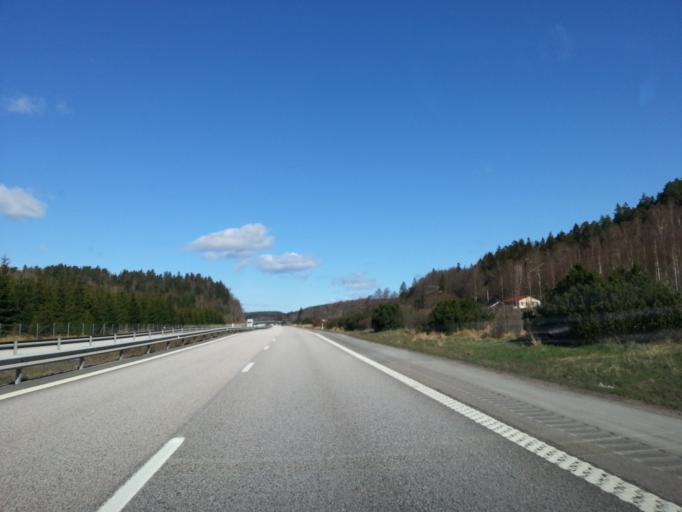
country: SE
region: Vaestra Goetaland
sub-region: Uddevalla Kommun
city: Ljungskile
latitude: 58.2664
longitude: 11.8947
